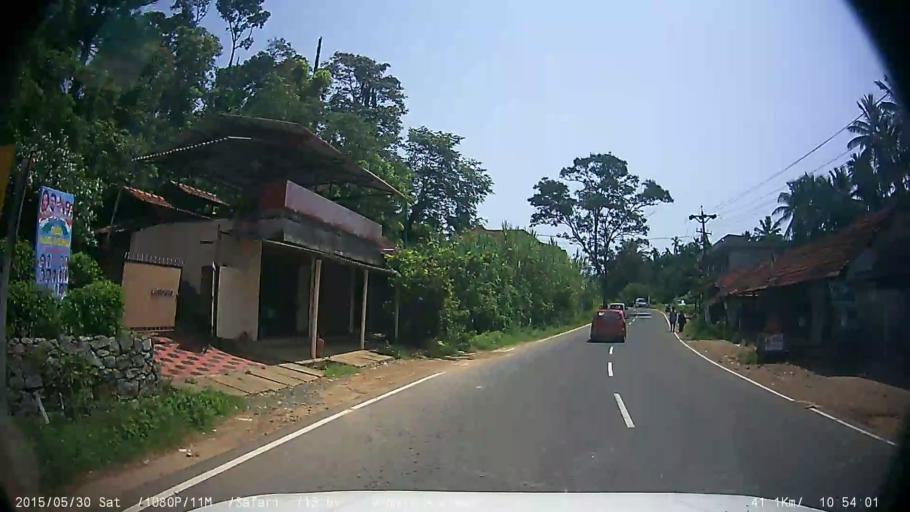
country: IN
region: Kerala
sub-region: Wayanad
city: Kalpetta
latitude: 11.6621
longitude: 76.0841
